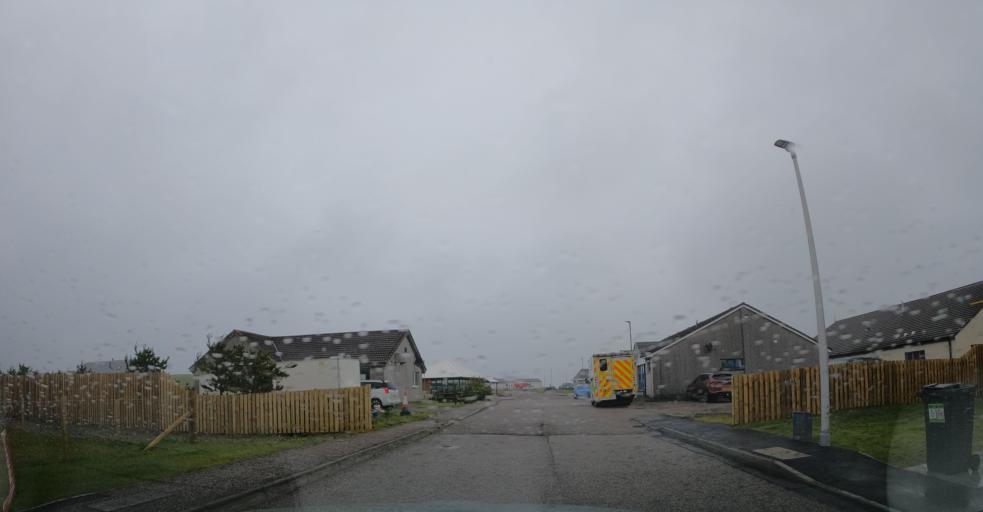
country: GB
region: Scotland
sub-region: Eilean Siar
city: Benbecula
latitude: 57.4722
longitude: -7.3786
